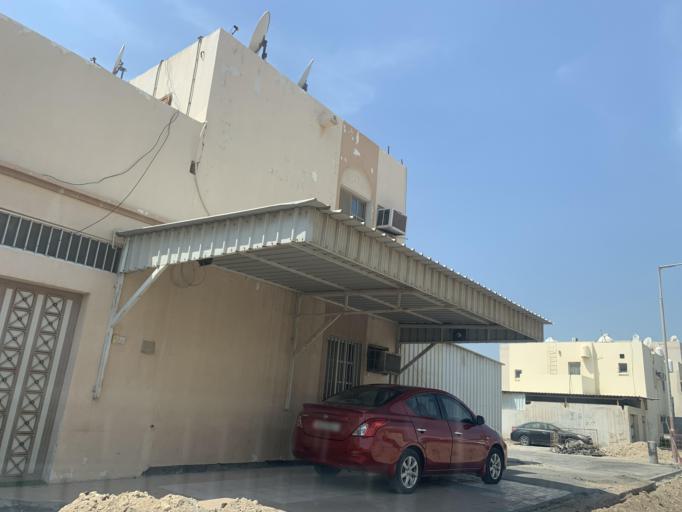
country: BH
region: Central Governorate
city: Madinat Hamad
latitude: 26.1346
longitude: 50.5008
